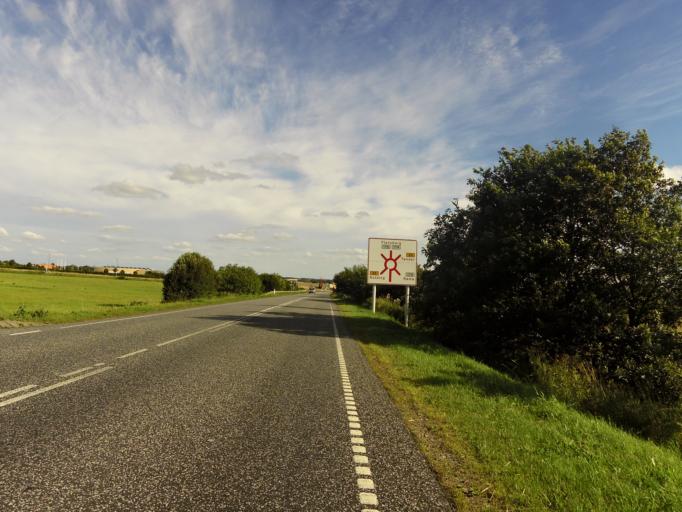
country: DK
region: South Denmark
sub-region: Tonder Kommune
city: Toftlund
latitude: 55.1823
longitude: 9.0607
